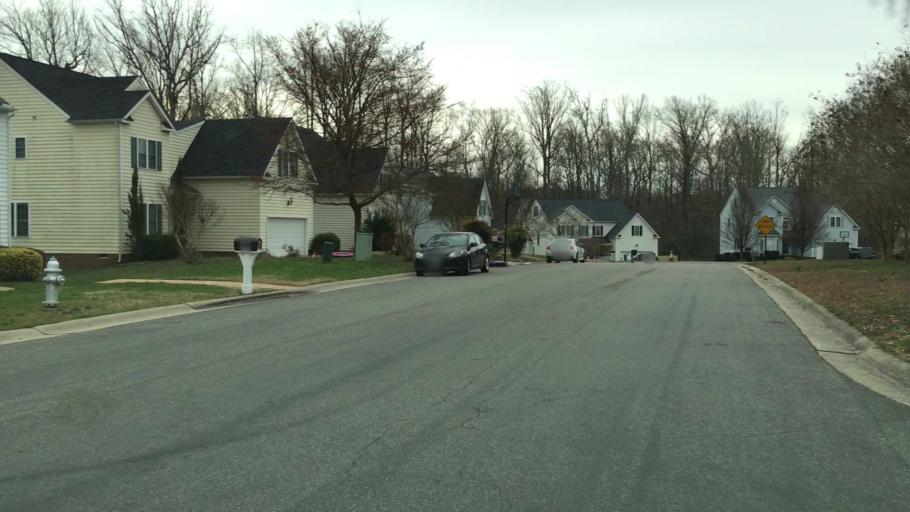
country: US
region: Virginia
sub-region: Henrico County
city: Short Pump
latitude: 37.6508
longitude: -77.5691
